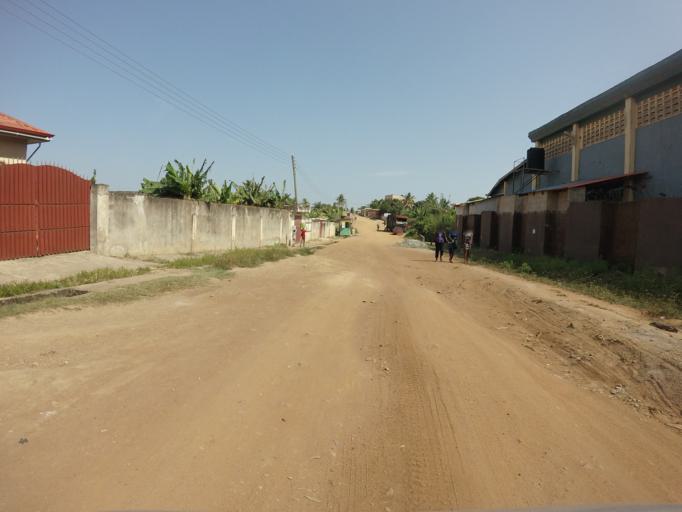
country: GH
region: Greater Accra
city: Dome
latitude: 5.6313
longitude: -0.2325
